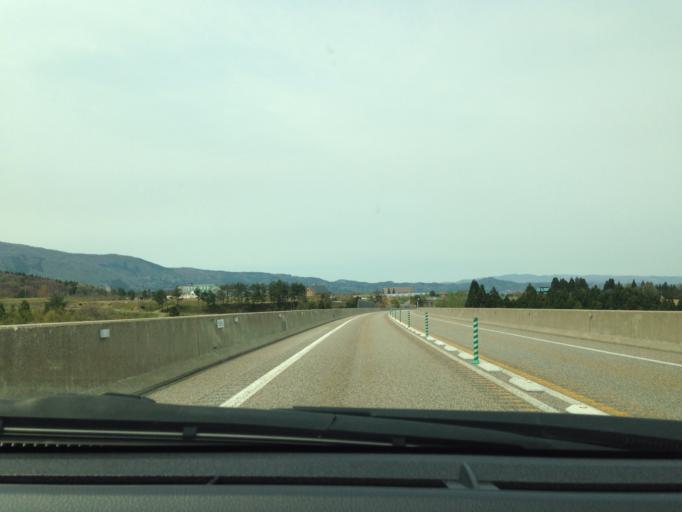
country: JP
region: Toyama
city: Fukumitsu
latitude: 36.4955
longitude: 136.8759
